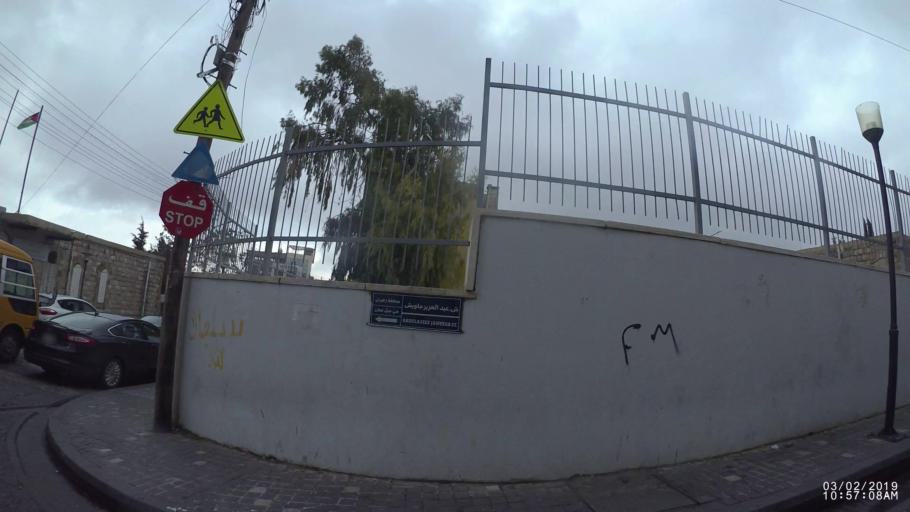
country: JO
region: Amman
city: Amman
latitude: 31.9493
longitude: 35.9265
